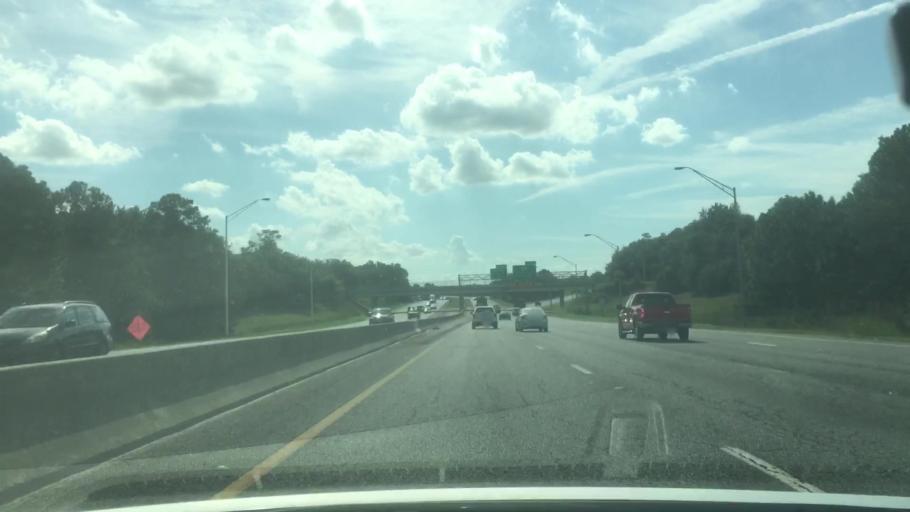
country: US
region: Florida
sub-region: Duval County
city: Jacksonville
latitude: 30.3640
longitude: -81.5535
